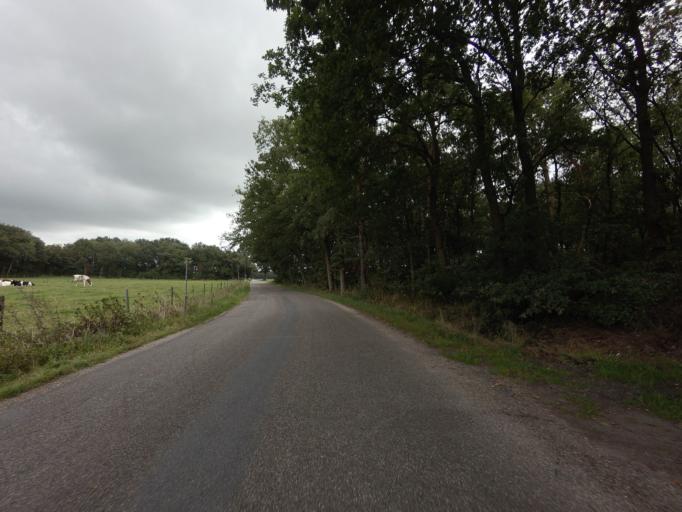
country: NL
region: Overijssel
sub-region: Gemeente Losser
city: Losser
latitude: 52.2580
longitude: 7.0246
